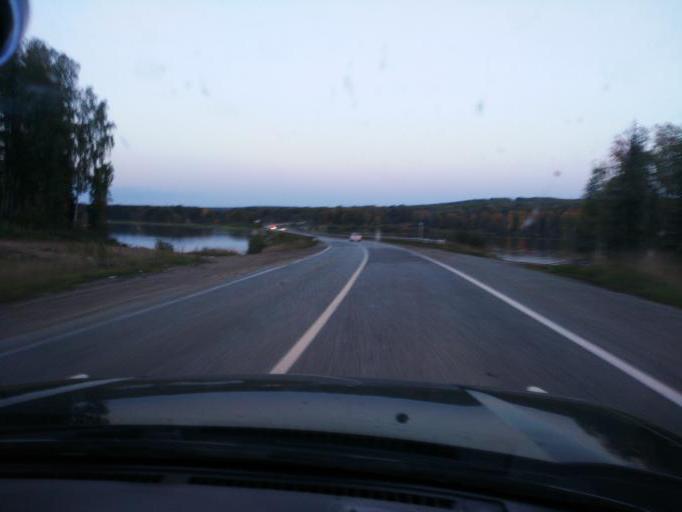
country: RU
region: Perm
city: Verkhnechusovskiye Gorodki
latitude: 58.2937
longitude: 56.8763
